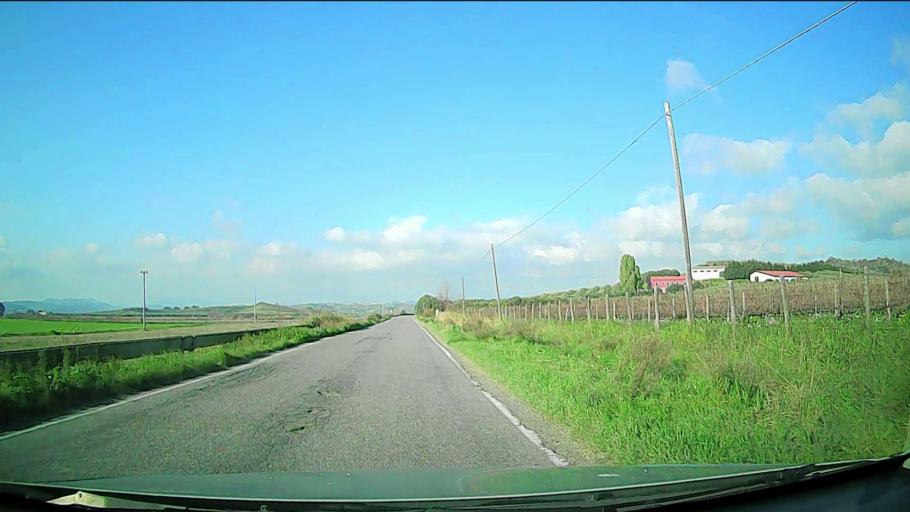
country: IT
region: Calabria
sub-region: Provincia di Crotone
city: Tronca
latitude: 39.1987
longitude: 17.0843
